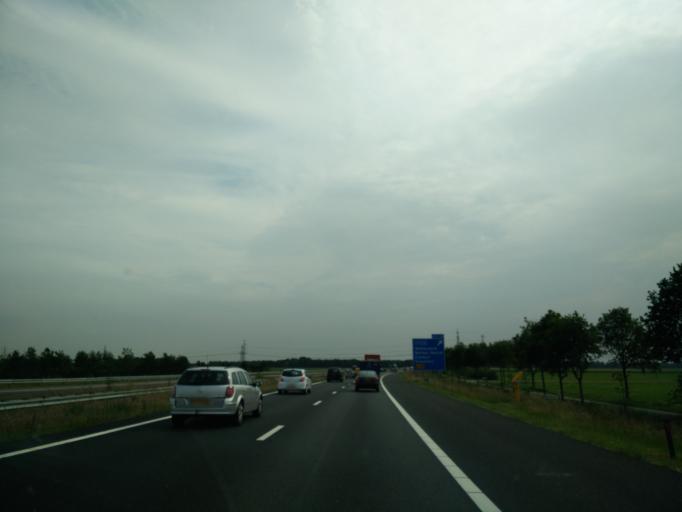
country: NL
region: Drenthe
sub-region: Gemeente Assen
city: Assen
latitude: 52.8885
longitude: 6.5258
